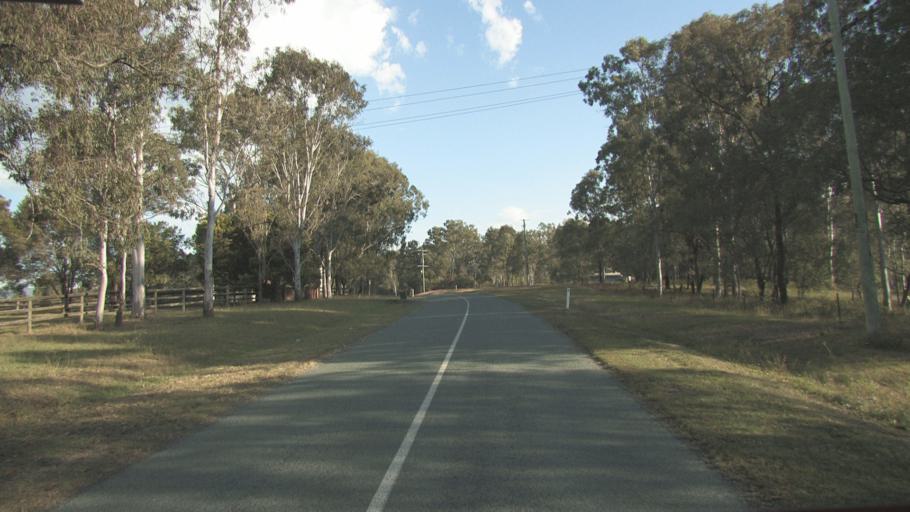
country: AU
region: Queensland
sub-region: Gold Coast
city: Ormeau Hills
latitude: -27.8314
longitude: 153.1705
